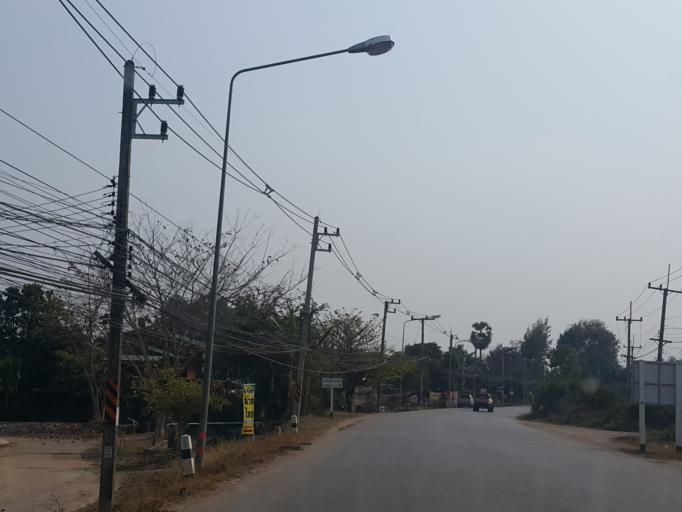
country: TH
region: Chiang Mai
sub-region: Amphoe Chiang Dao
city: Chiang Dao
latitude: 19.3575
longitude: 98.9644
